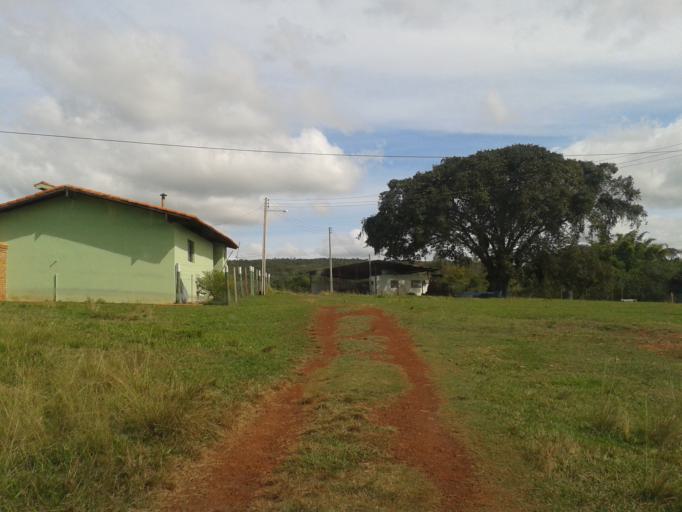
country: BR
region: Minas Gerais
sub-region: Campina Verde
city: Campina Verde
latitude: -19.4301
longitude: -49.7139
